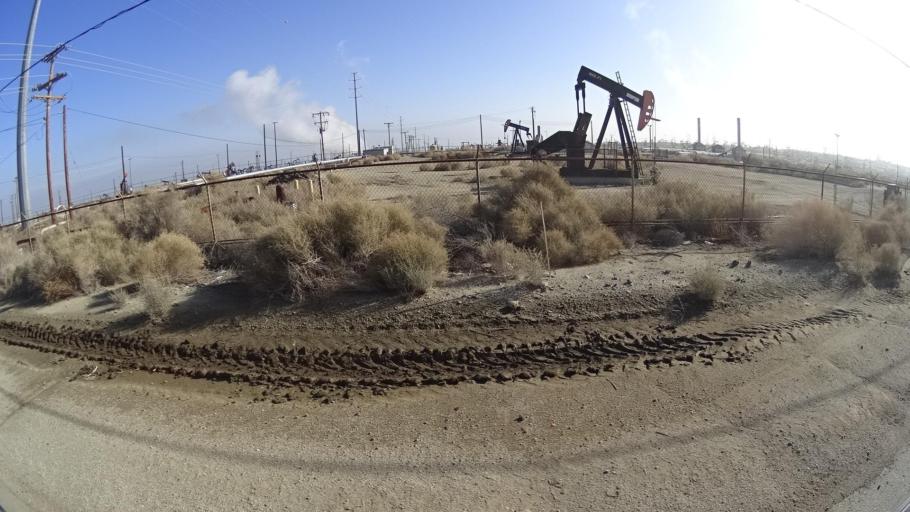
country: US
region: California
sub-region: Kern County
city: Taft Heights
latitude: 35.2090
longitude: -119.5981
